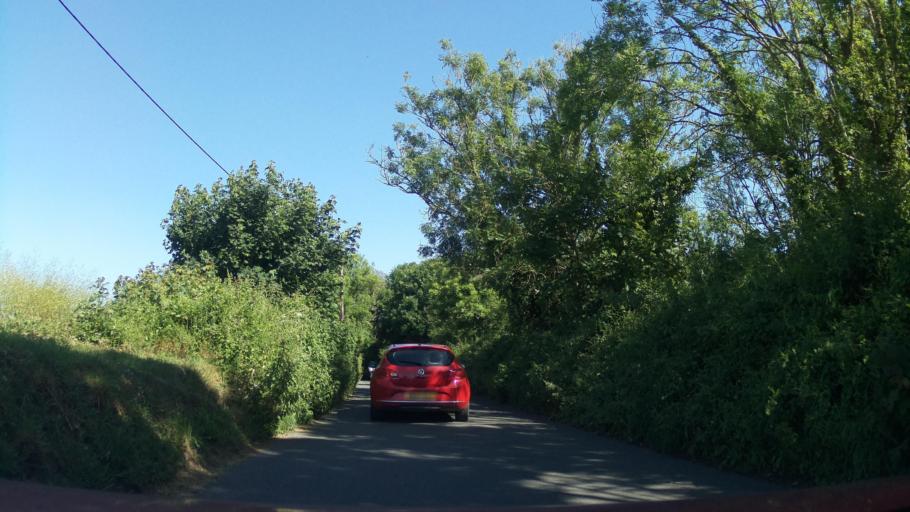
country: GB
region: England
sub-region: Borough of Torbay
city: Brixham
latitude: 50.3984
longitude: -3.5519
